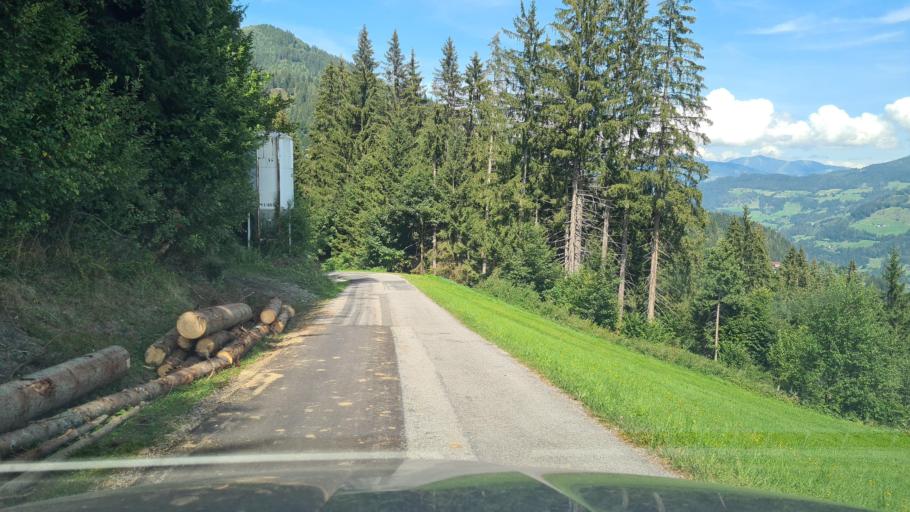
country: AT
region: Salzburg
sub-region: Politischer Bezirk Sankt Johann im Pongau
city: Sankt Johann im Pongau
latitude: 47.3578
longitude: 13.1824
